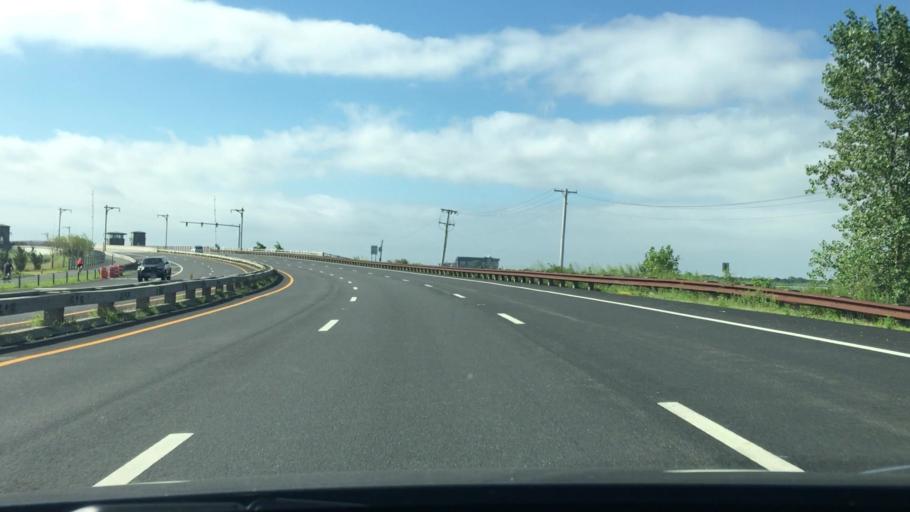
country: US
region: New York
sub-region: Nassau County
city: Seaford
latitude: 40.6169
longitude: -73.5023
